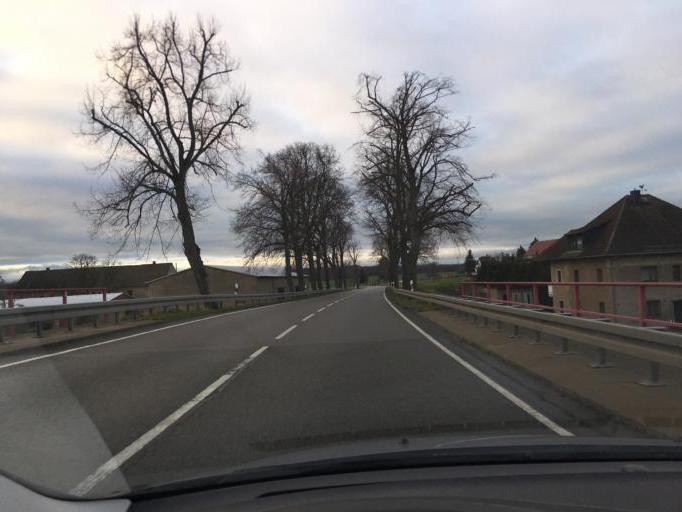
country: DE
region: Saxony
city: Frohburg
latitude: 51.0115
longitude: 12.5622
